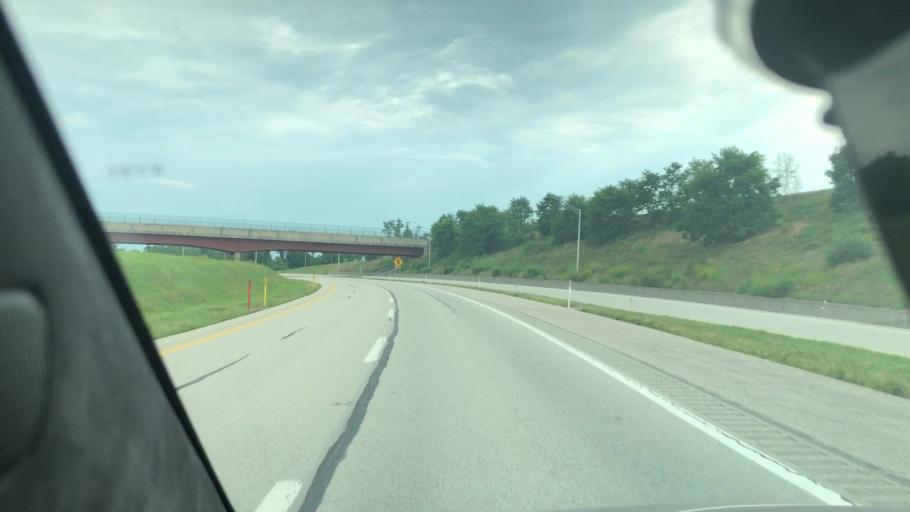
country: US
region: Pennsylvania
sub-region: Washington County
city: Baidland
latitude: 40.1912
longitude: -79.9895
